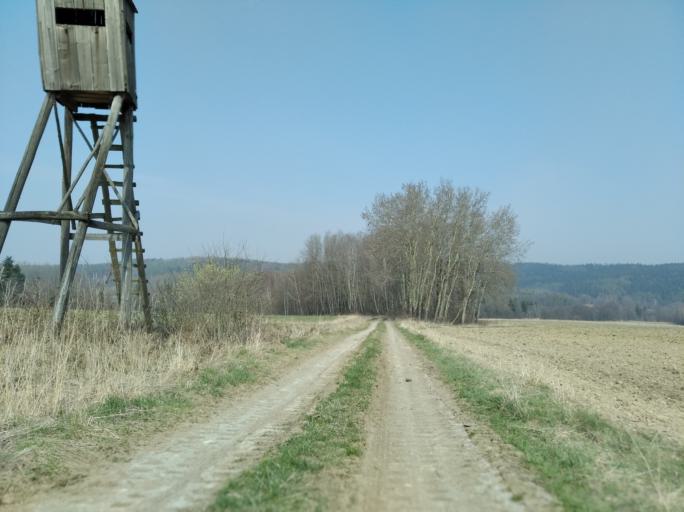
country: PL
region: Subcarpathian Voivodeship
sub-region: Powiat krosnienski
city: Korczyna
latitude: 49.7920
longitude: 21.8073
